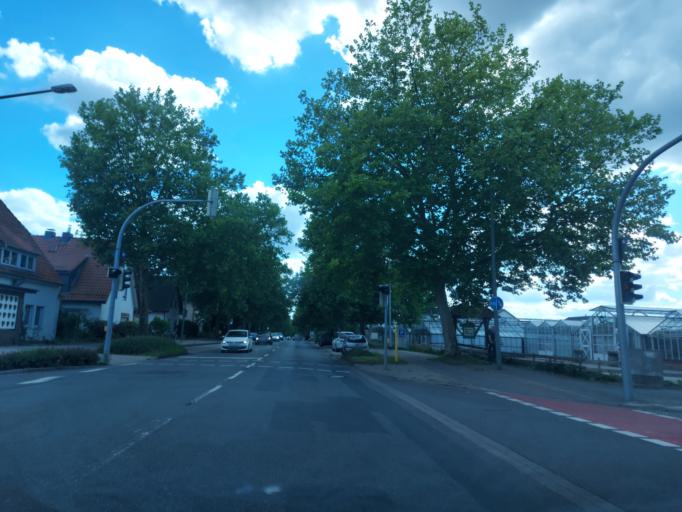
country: DE
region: Lower Saxony
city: Osnabrueck
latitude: 52.2402
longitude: 8.0313
